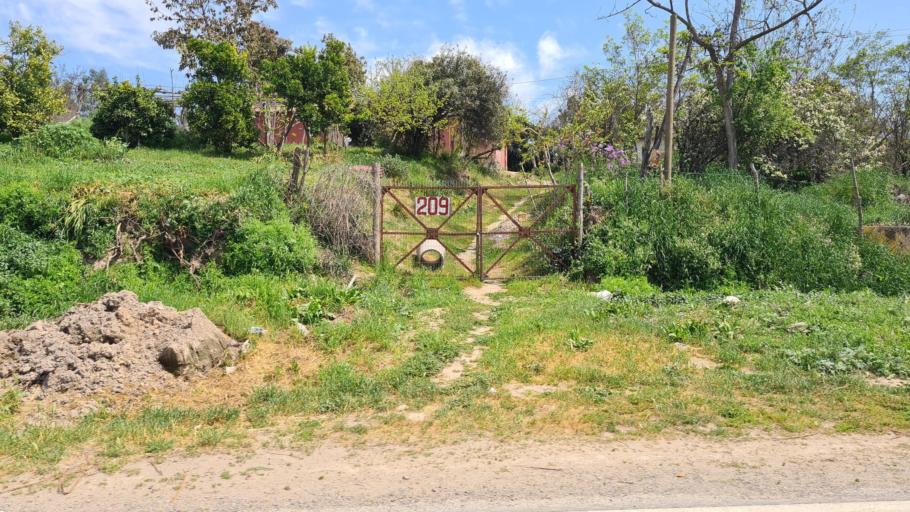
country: CL
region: O'Higgins
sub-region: Provincia de Cachapoal
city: San Vicente
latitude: -34.1708
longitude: -71.4070
